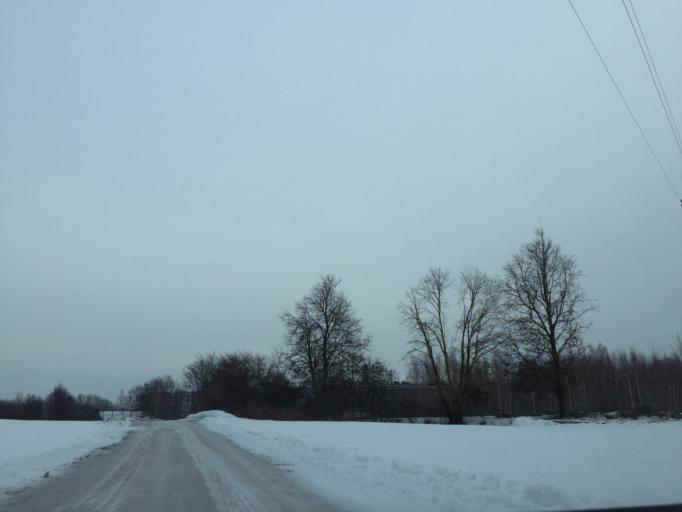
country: LV
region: Ikskile
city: Ikskile
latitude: 56.8478
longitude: 24.4372
